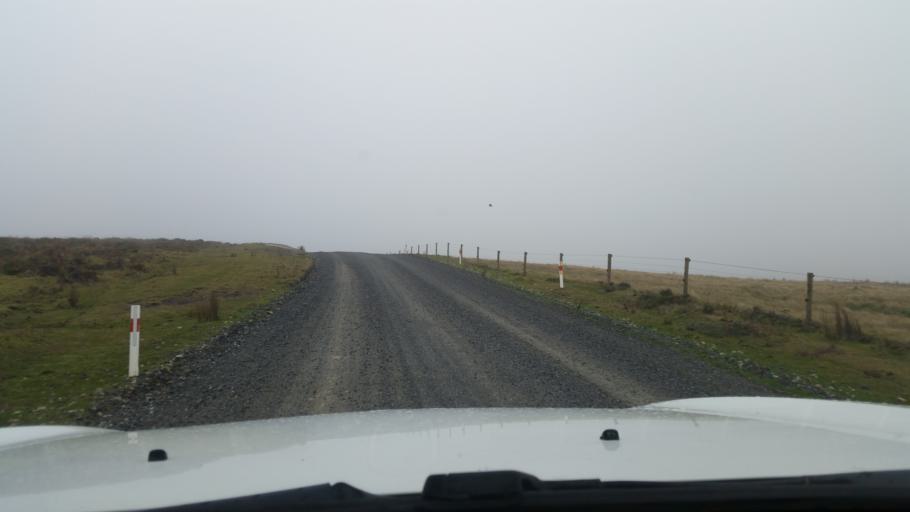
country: NZ
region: Chatham Islands
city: Waitangi
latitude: -43.8021
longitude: -176.6308
